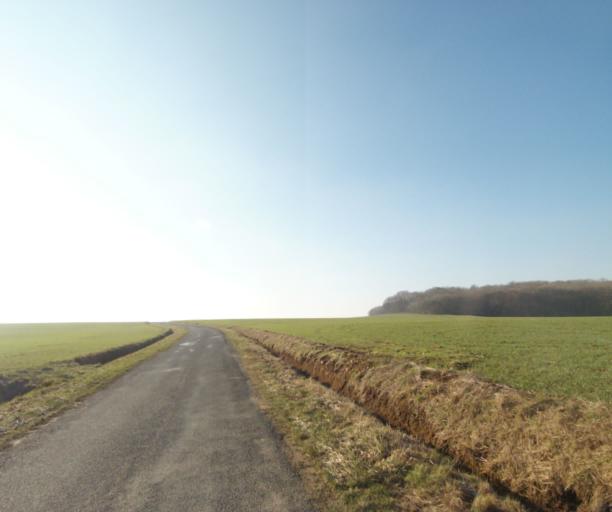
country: FR
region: Champagne-Ardenne
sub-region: Departement de la Haute-Marne
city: Bienville
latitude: 48.5471
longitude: 5.0350
